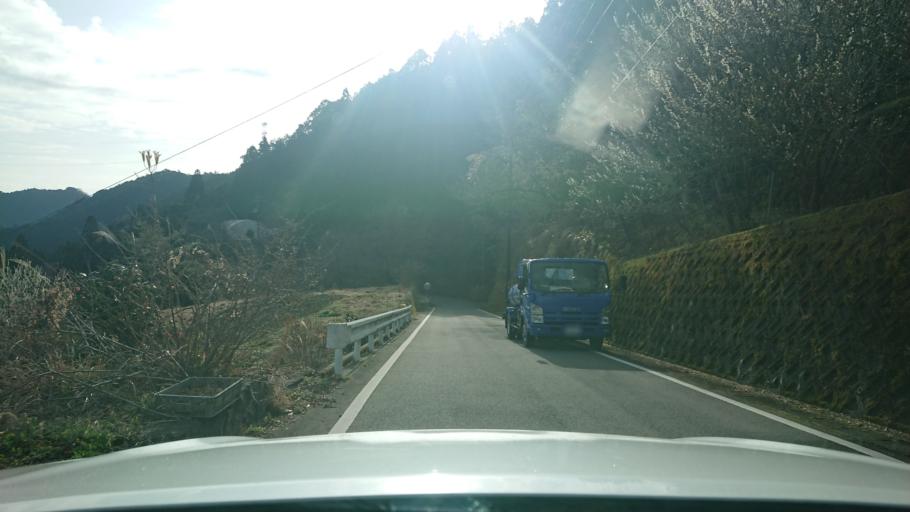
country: JP
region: Tokushima
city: Ishii
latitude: 33.9145
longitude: 134.4127
